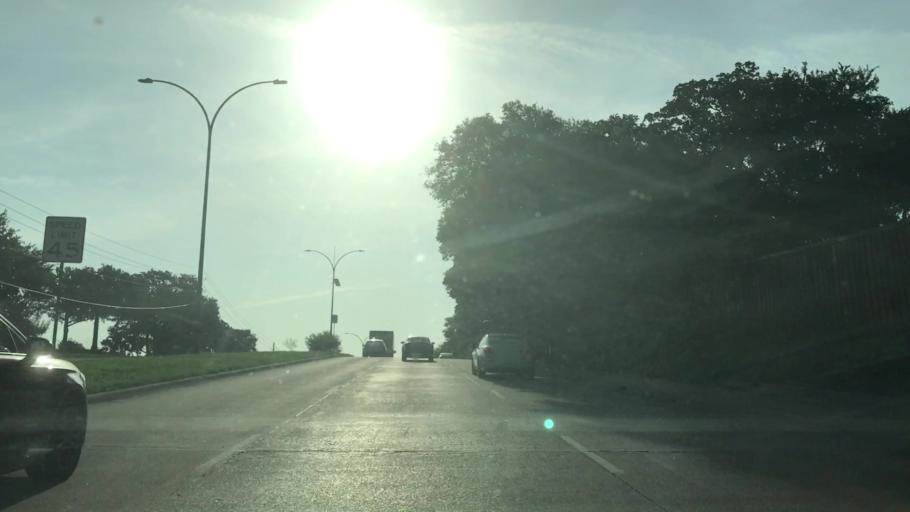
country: US
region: Texas
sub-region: Tarrant County
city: Arlington
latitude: 32.7852
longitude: -97.1056
